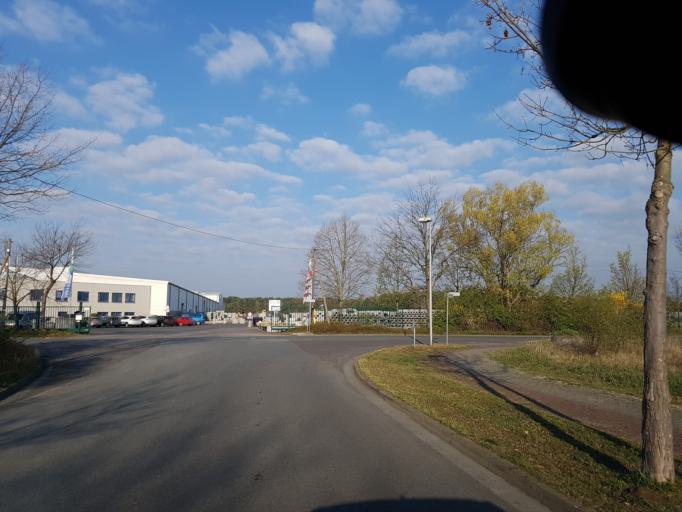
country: DE
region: Brandenburg
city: Linthe
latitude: 52.1681
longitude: 12.7763
